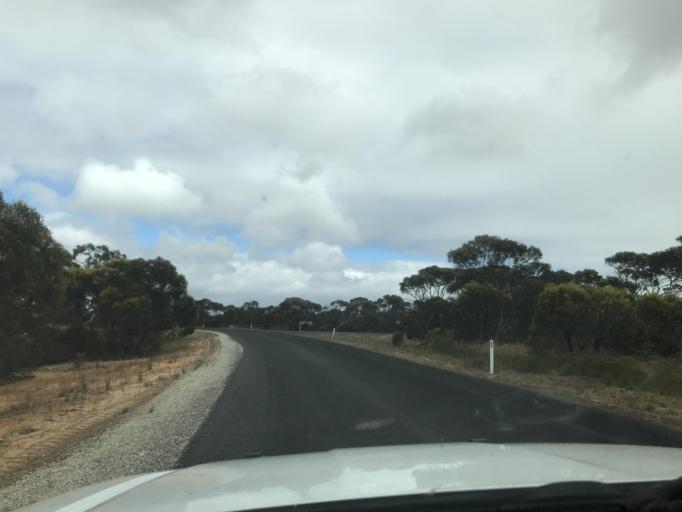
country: AU
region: South Australia
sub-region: Tatiara
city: Bordertown
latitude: -36.1321
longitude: 141.1599
